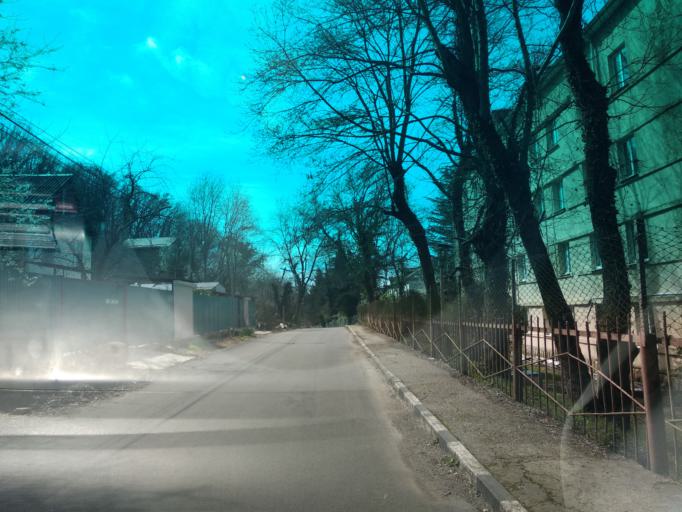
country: RU
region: Krasnodarskiy
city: Shepsi
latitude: 44.0358
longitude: 39.1488
